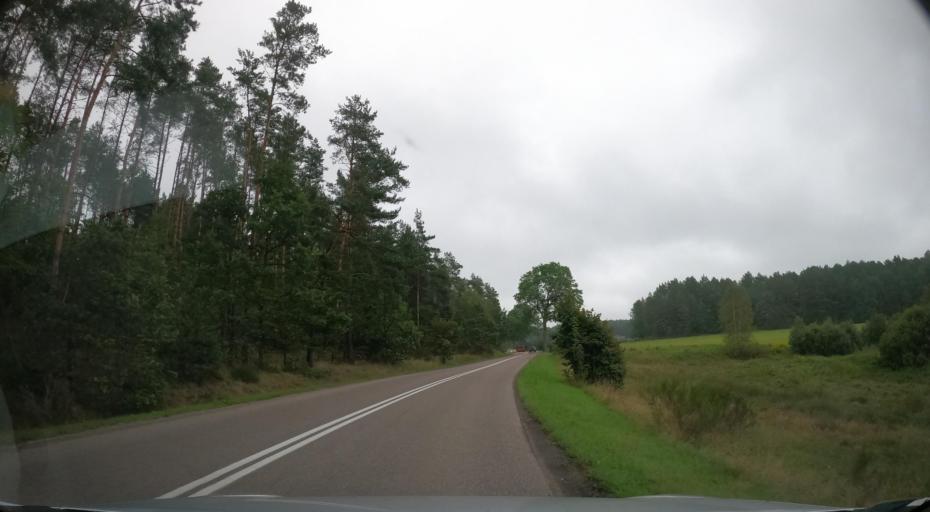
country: PL
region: Pomeranian Voivodeship
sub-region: Powiat wejherowski
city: Luzino
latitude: 54.4747
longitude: 18.0839
